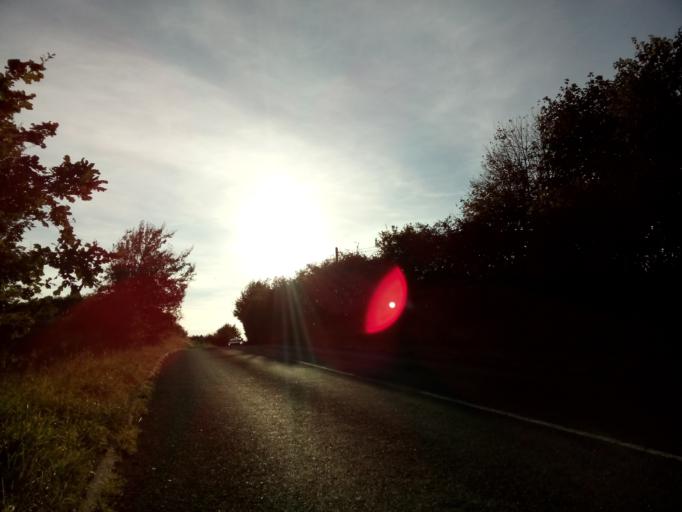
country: GB
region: England
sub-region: Suffolk
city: Bramford
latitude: 52.0309
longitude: 1.1128
